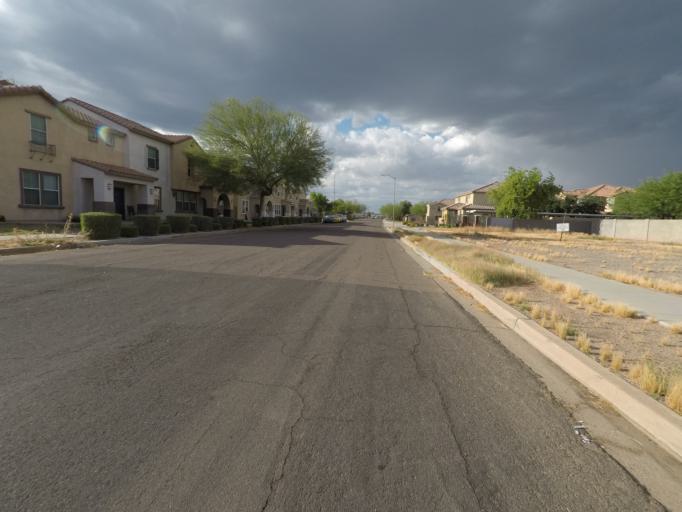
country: US
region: Arizona
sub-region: Maricopa County
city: Phoenix
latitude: 33.4380
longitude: -112.0891
